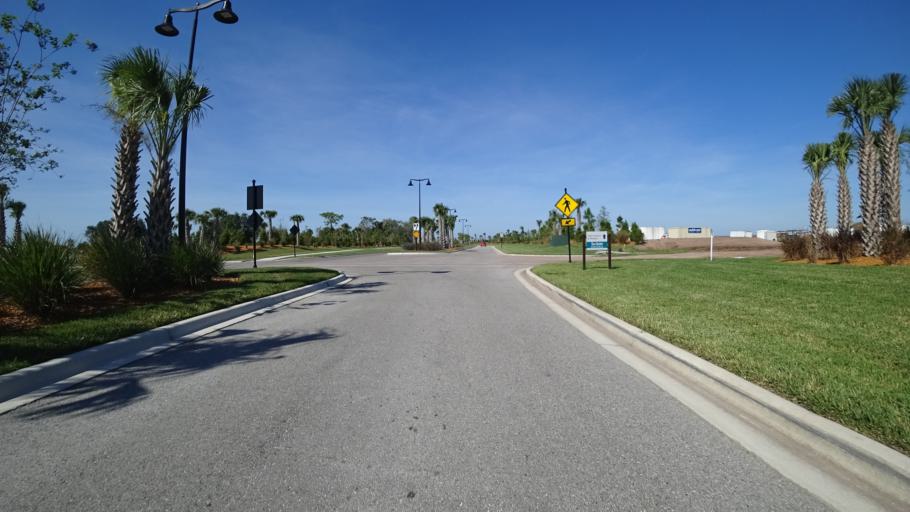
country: US
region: Florida
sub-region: Sarasota County
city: The Meadows
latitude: 27.4039
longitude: -82.3581
